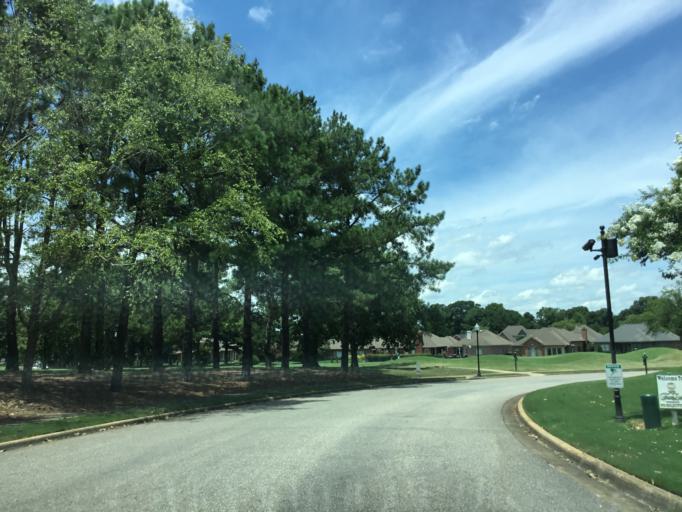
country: US
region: Alabama
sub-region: Montgomery County
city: Pike Road
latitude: 32.3722
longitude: -86.1367
